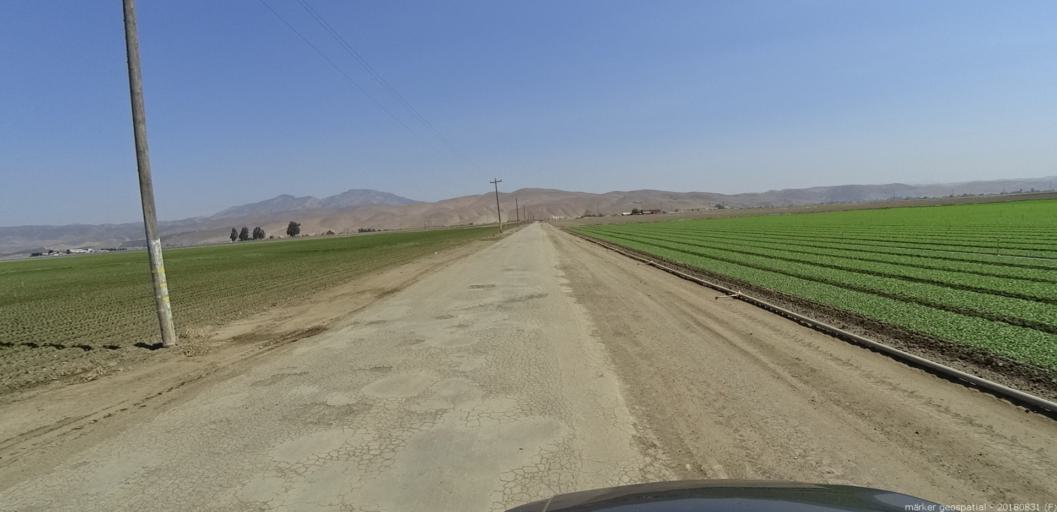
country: US
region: California
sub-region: Monterey County
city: Greenfield
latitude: 36.3560
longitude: -121.2612
